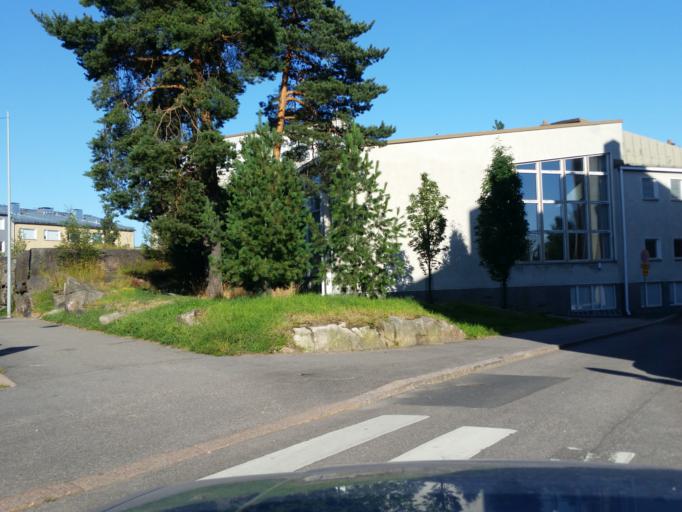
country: FI
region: Uusimaa
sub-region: Helsinki
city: Helsinki
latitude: 60.1928
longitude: 24.9384
